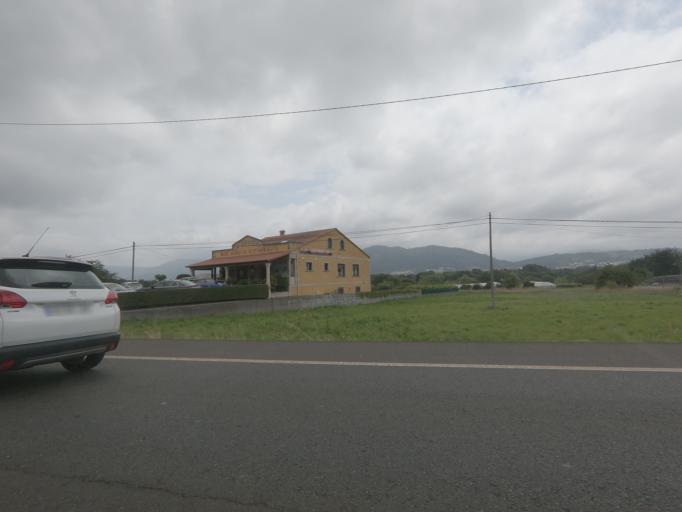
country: ES
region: Galicia
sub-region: Provincia de Pontevedra
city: O Rosal
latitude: 41.9228
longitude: -8.8097
